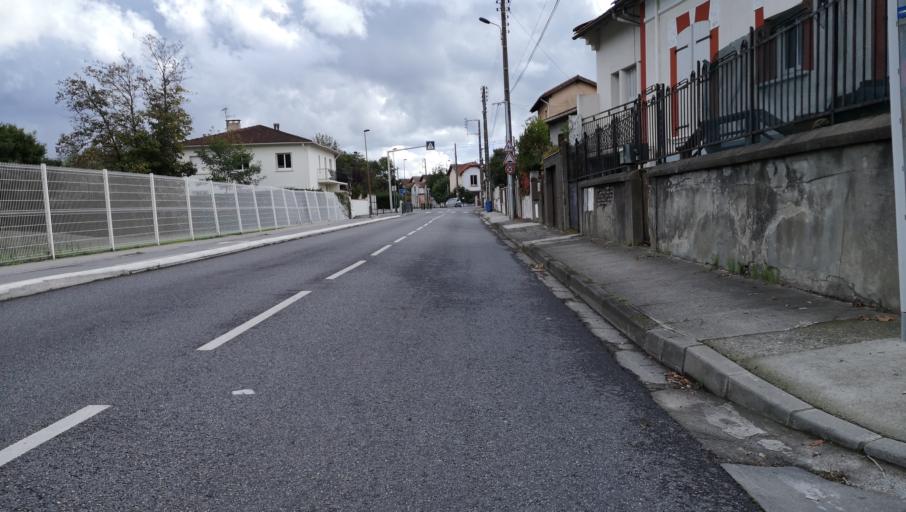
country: FR
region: Midi-Pyrenees
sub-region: Departement de la Haute-Garonne
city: Blagnac
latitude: 43.6093
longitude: 1.4065
